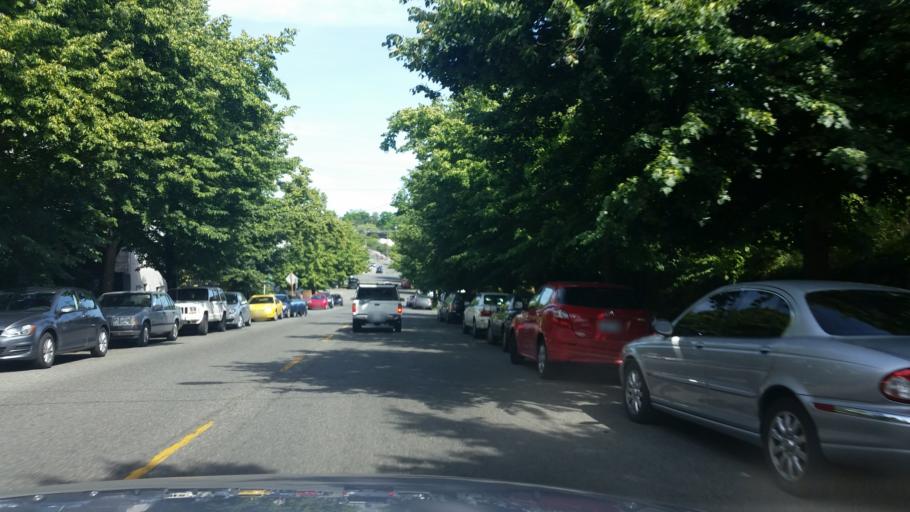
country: US
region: Washington
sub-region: King County
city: Seattle
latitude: 47.6499
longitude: -122.3456
